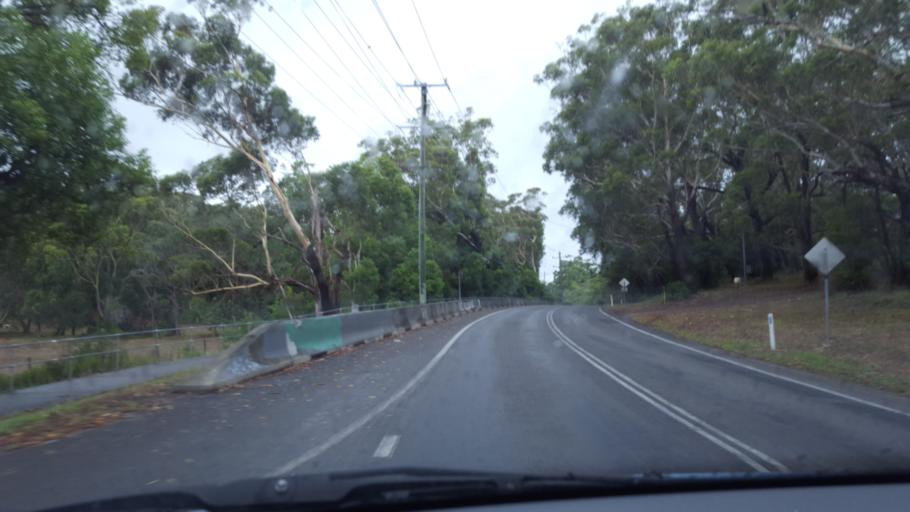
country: AU
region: New South Wales
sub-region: Port Stephens Shire
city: Anna Bay
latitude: -32.7762
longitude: 152.0936
